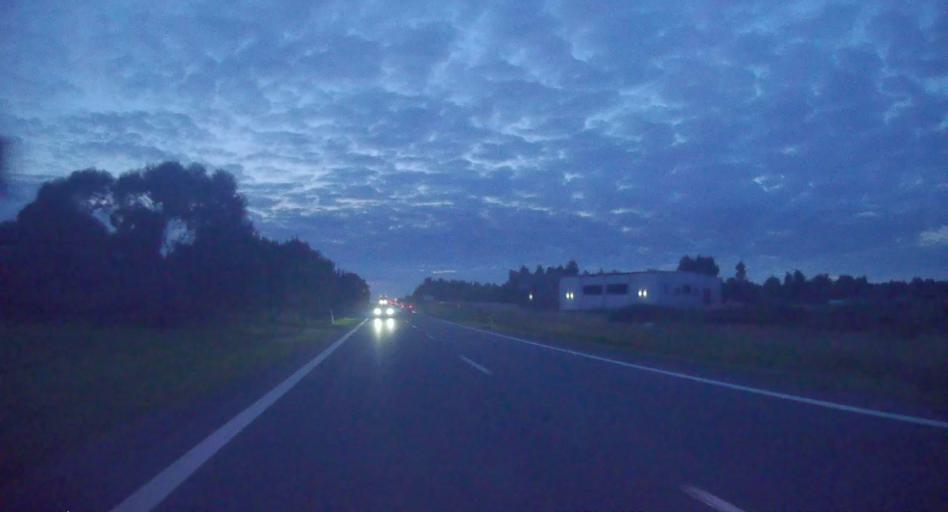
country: PL
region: Silesian Voivodeship
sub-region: Powiat klobucki
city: Kamyk
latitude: 50.8596
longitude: 19.0258
